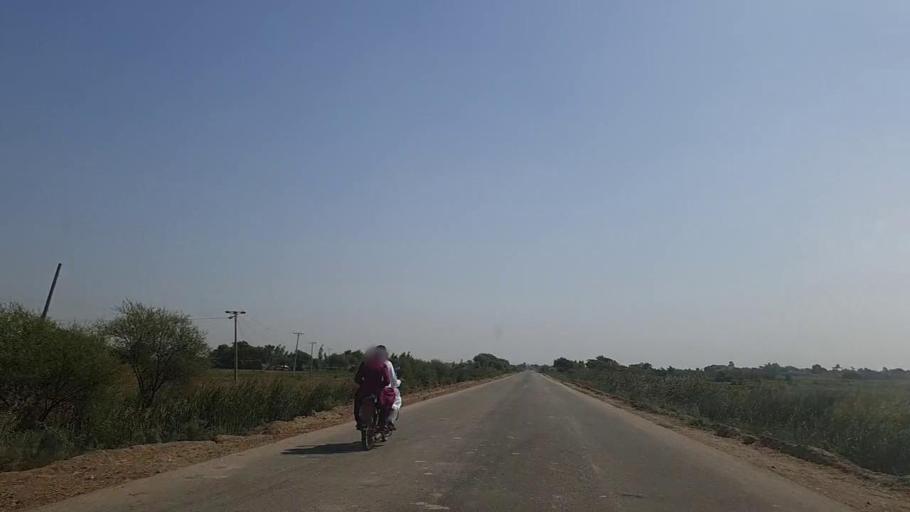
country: PK
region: Sindh
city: Daro Mehar
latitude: 24.7743
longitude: 68.2059
